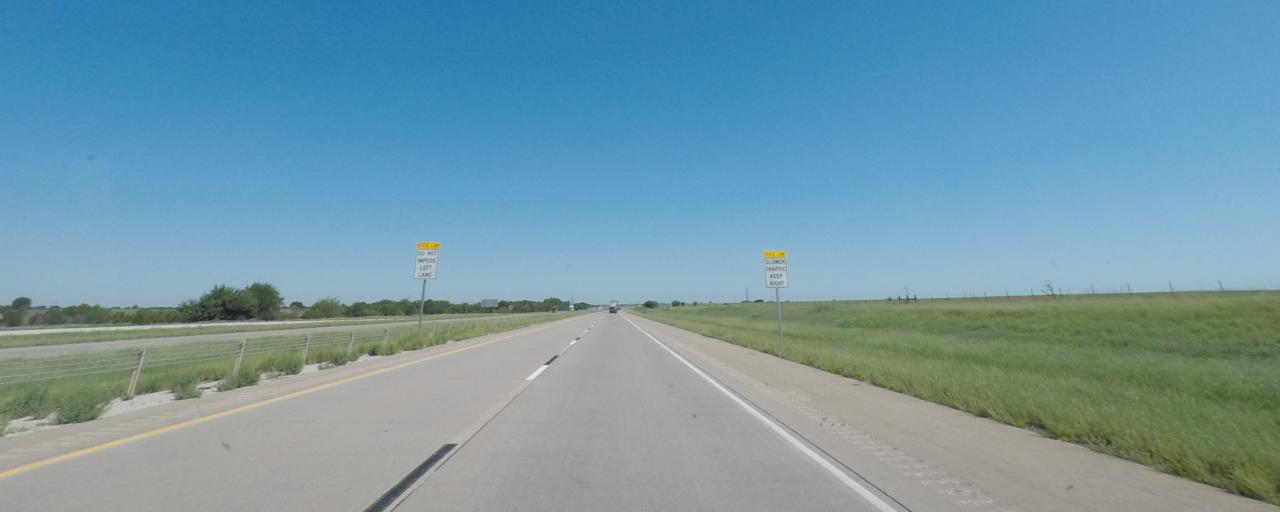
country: US
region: Oklahoma
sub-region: Noble County
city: Perry
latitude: 36.4132
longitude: -97.3269
